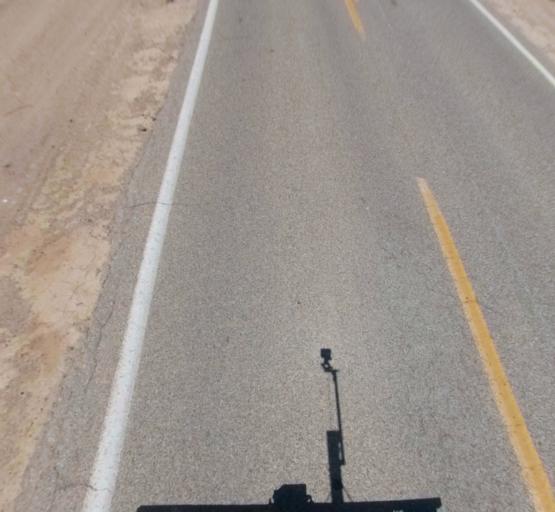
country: US
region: California
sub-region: Madera County
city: Fairmead
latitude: 37.0184
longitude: -120.2137
